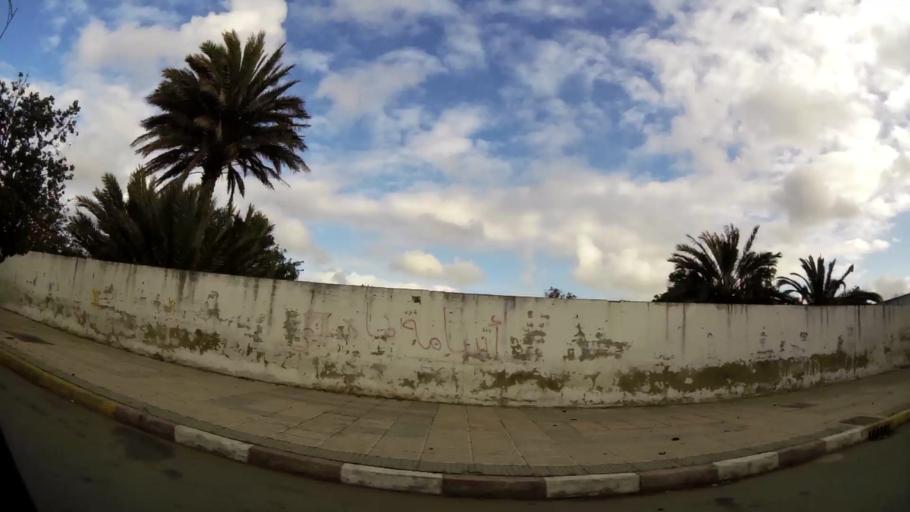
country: MA
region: Grand Casablanca
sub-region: Mohammedia
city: Mohammedia
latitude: 33.7016
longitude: -7.3766
